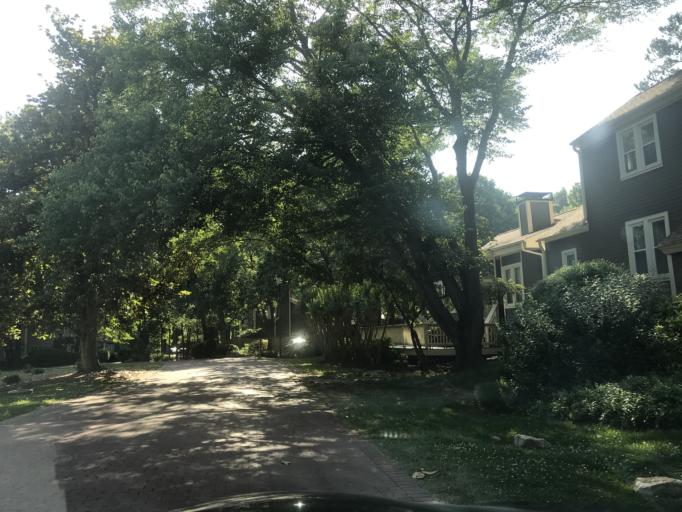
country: US
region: North Carolina
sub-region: Wake County
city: West Raleigh
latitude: 35.8638
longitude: -78.6095
